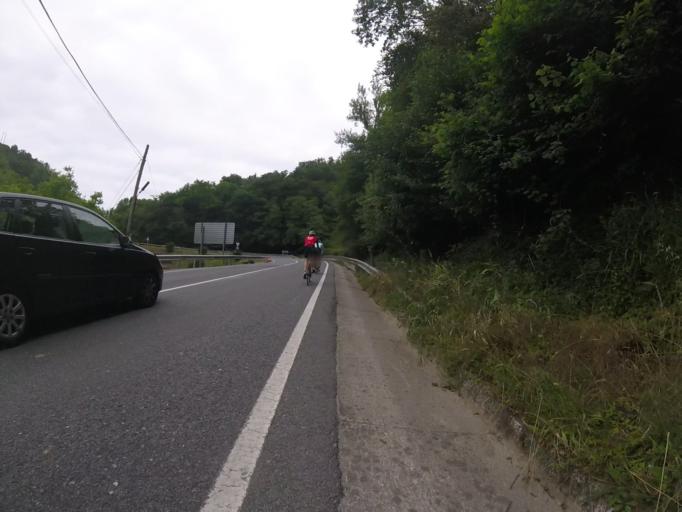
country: ES
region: Basque Country
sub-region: Provincia de Guipuzcoa
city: Orio
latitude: 43.2777
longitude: -2.1130
